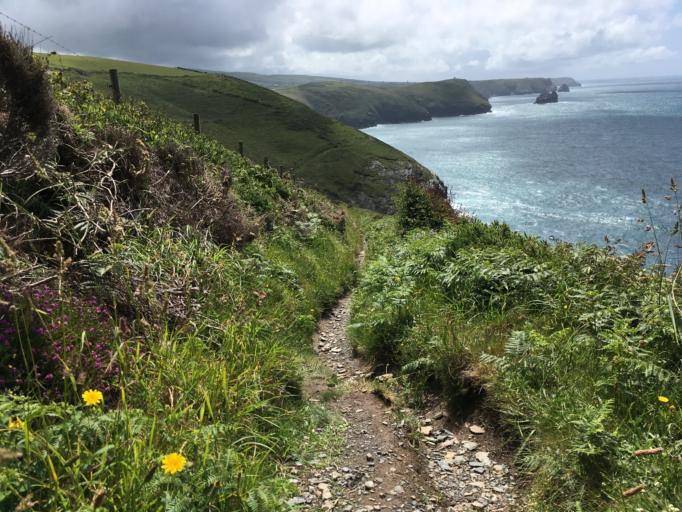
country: GB
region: England
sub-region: Cornwall
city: Tintagel
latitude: 50.7038
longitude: -4.6805
